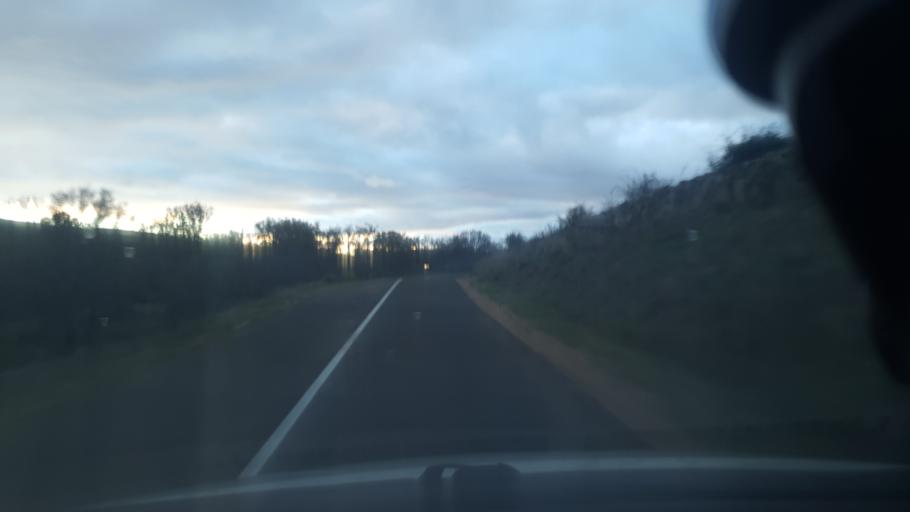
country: ES
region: Castille and Leon
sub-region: Provincia de Segovia
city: Vegas de Matute
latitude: 40.7255
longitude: -4.2902
